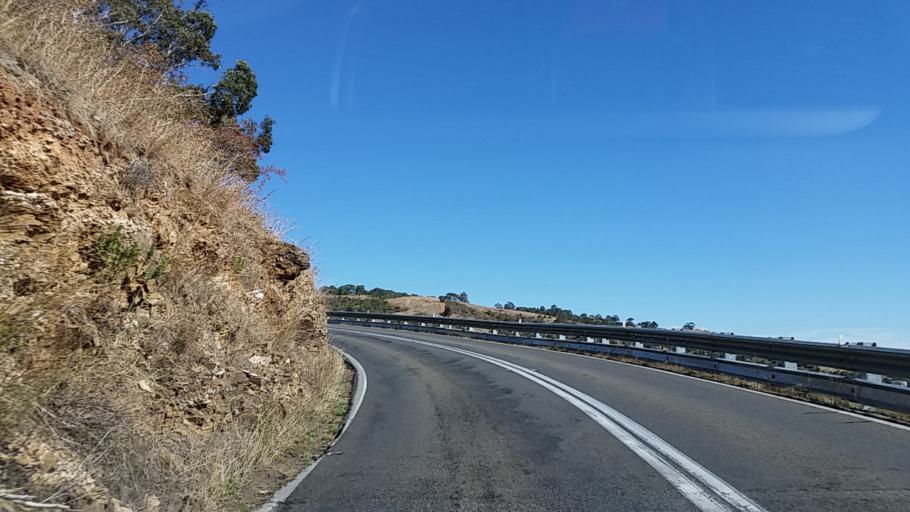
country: AU
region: South Australia
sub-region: Burnside
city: Beaumont
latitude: -34.9480
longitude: 138.6721
